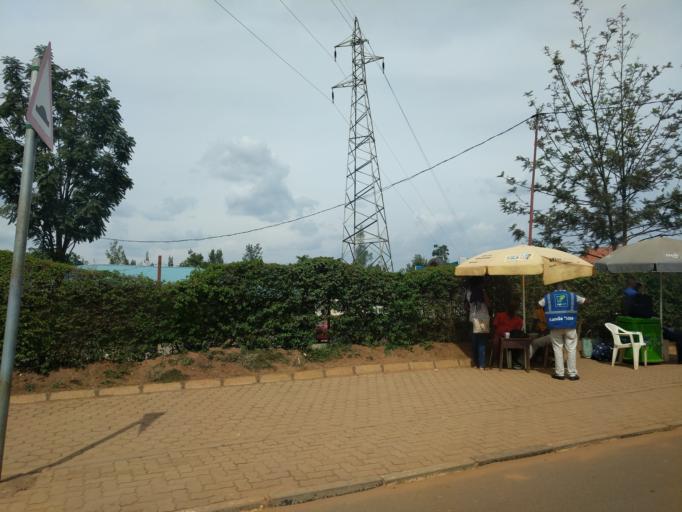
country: RW
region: Kigali
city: Kigali
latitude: -1.9818
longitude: 30.1175
